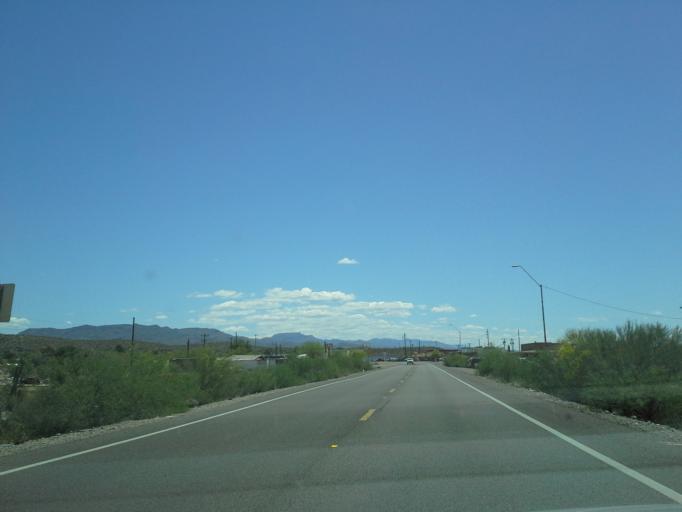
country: US
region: Arizona
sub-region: Pinal County
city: Kearny
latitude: 32.9903
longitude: -110.7793
